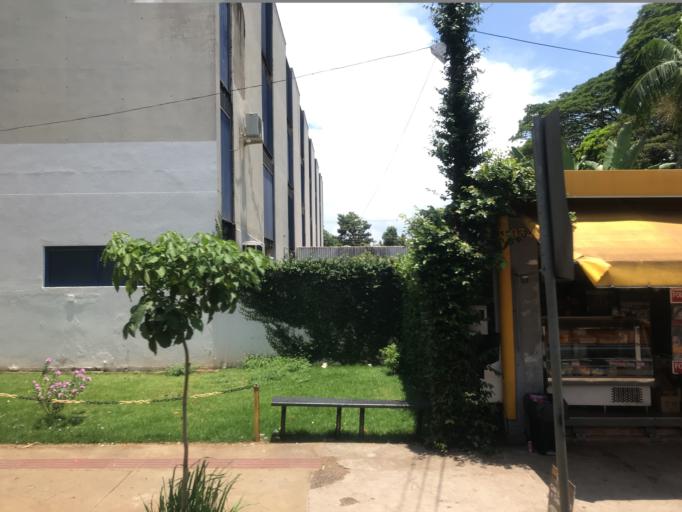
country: BR
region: Parana
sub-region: Londrina
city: Londrina
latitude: -23.3271
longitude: -51.1575
